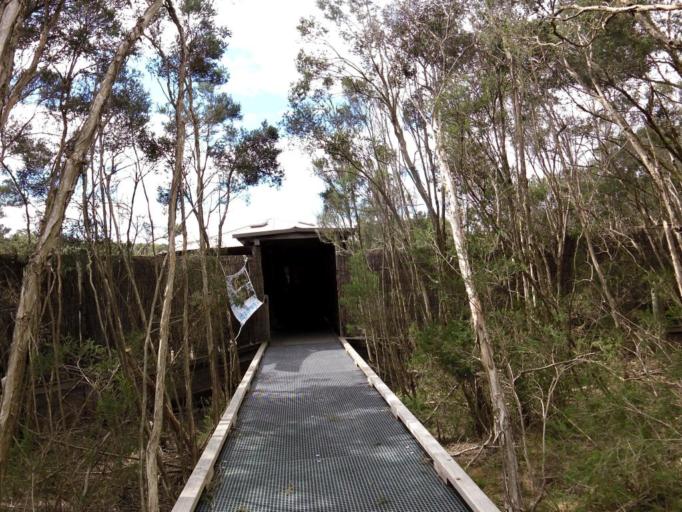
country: AU
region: Victoria
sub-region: Mornington Peninsula
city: Mount Martha
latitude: -38.2691
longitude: 145.0468
